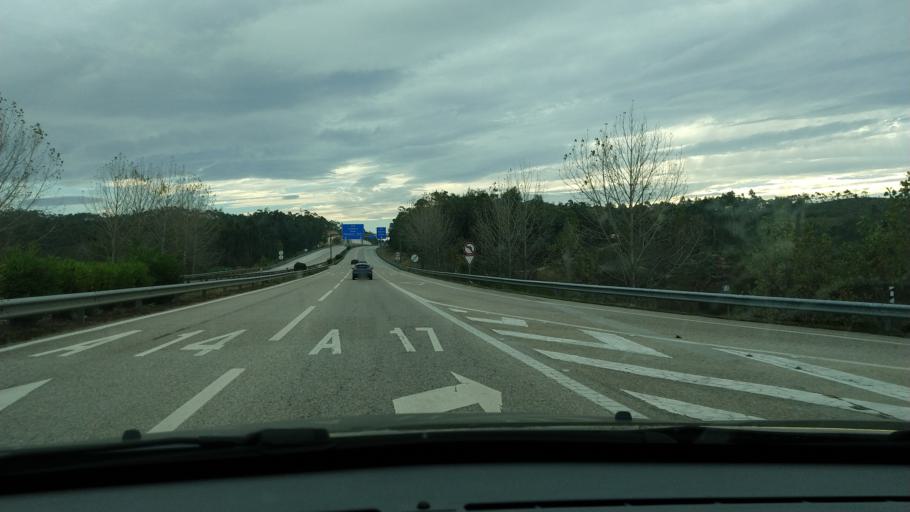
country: PT
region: Coimbra
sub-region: Figueira da Foz
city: Alhadas
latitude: 40.1537
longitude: -8.7927
